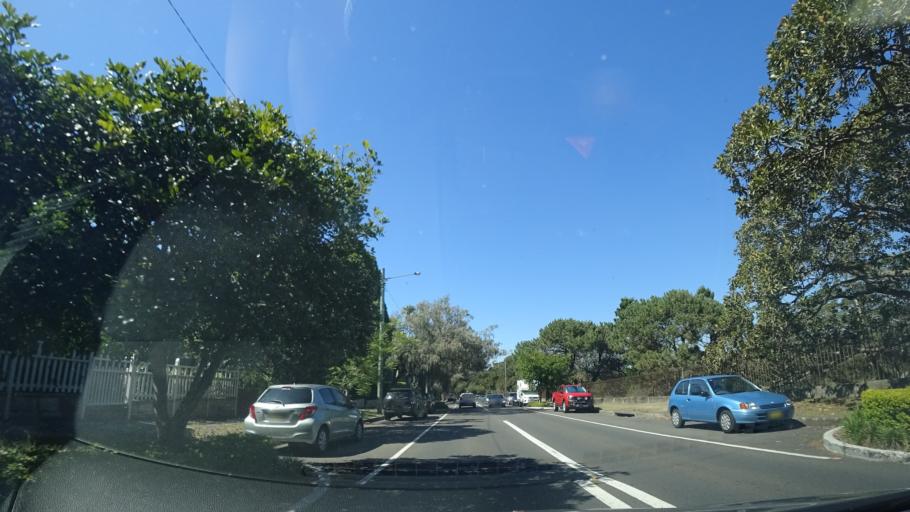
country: AU
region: New South Wales
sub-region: Waverley
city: Bondi Junction
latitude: -33.8932
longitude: 151.2412
